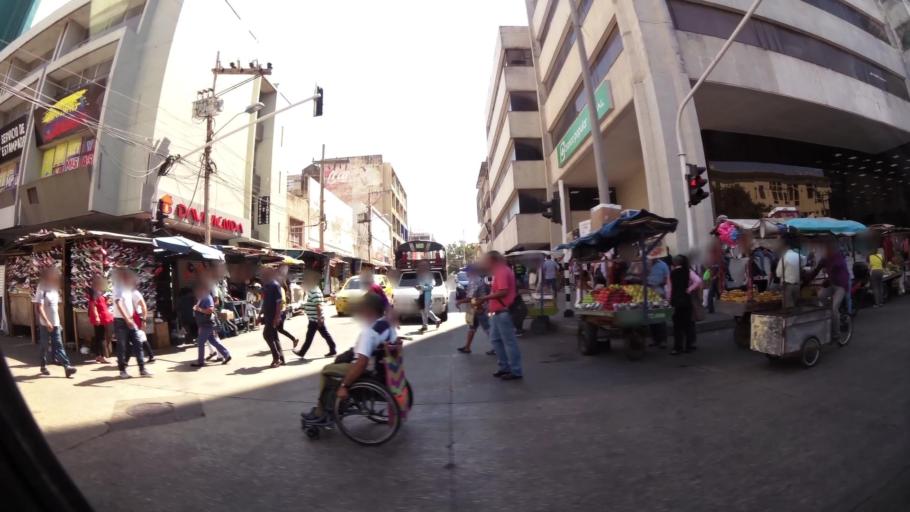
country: CO
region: Atlantico
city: Barranquilla
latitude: 10.9834
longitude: -74.7806
